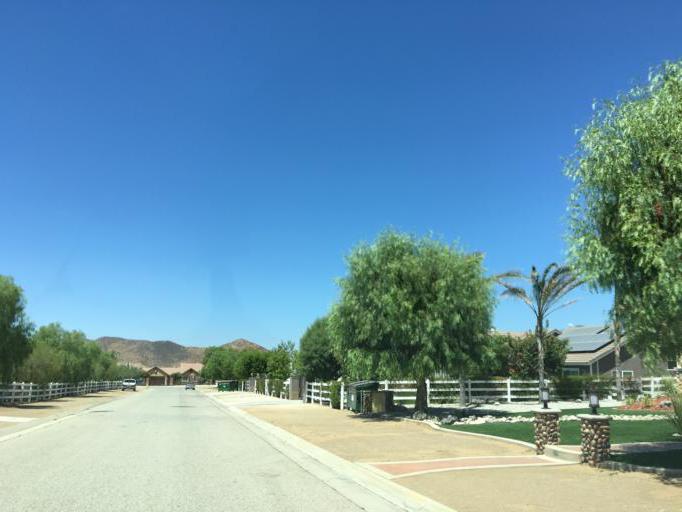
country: US
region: California
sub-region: Los Angeles County
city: Agua Dulce
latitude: 34.5131
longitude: -118.3056
